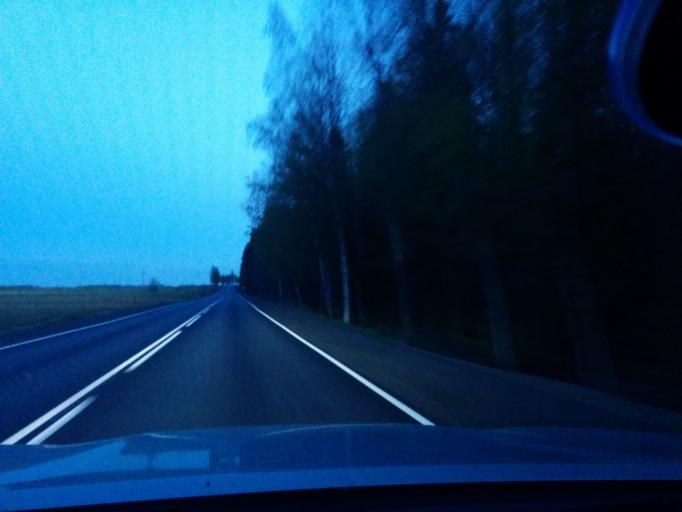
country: RU
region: Leningrad
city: Verkhniye Osel'ki
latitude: 60.1931
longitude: 30.4148
